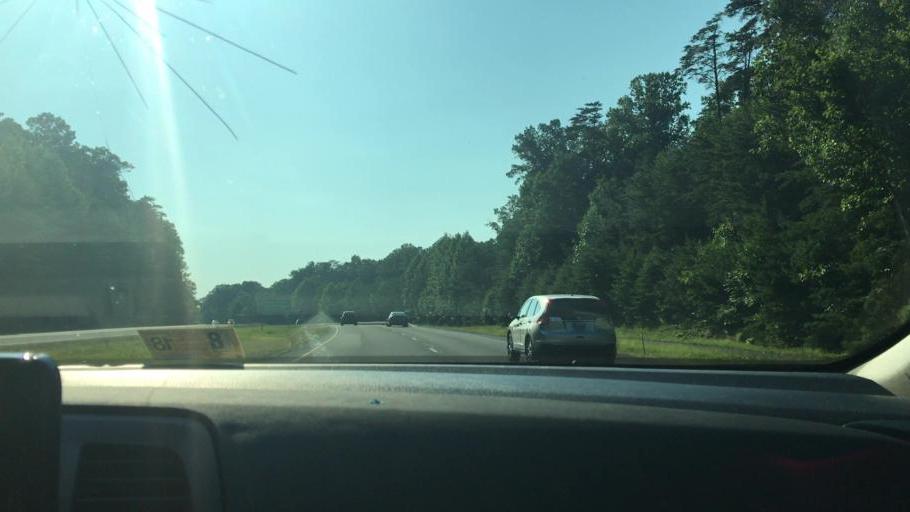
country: US
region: Virginia
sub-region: Prince William County
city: Buckhall
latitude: 38.6970
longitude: -77.3956
